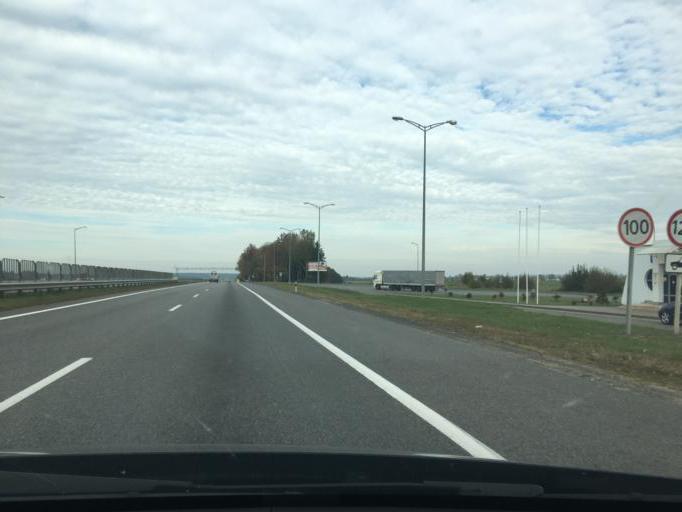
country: BY
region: Minsk
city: Enyerhyetykaw
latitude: 53.5960
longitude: 27.0427
